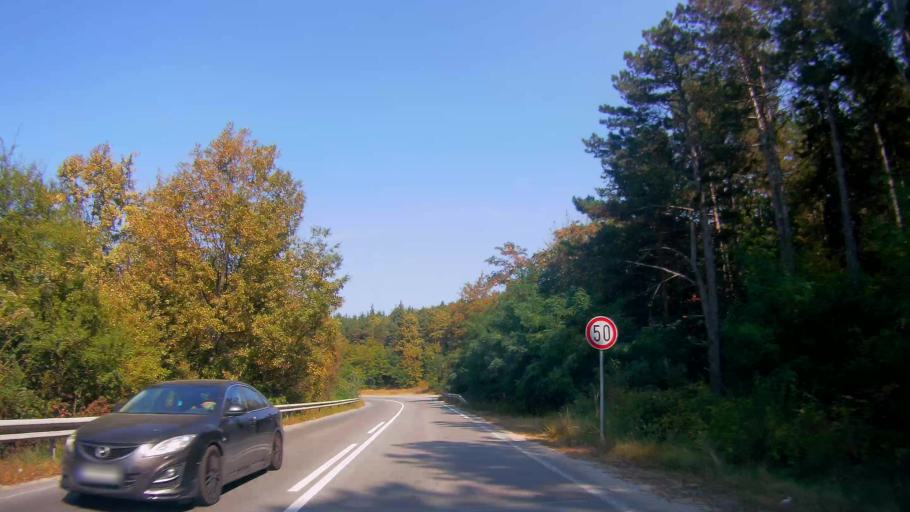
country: BG
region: Shumen
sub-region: Obshtina Smyadovo
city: Smyadovo
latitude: 42.9443
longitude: 26.9388
